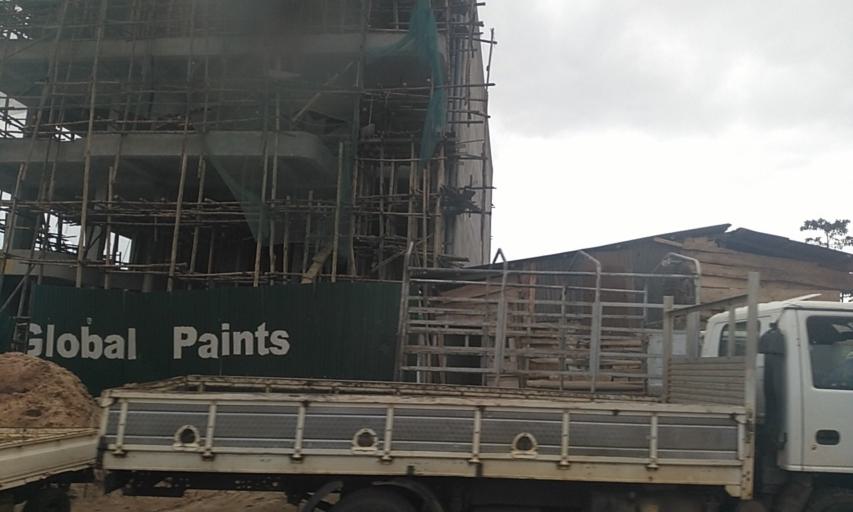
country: UG
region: Central Region
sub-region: Wakiso District
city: Kireka
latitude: 0.3460
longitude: 32.6469
